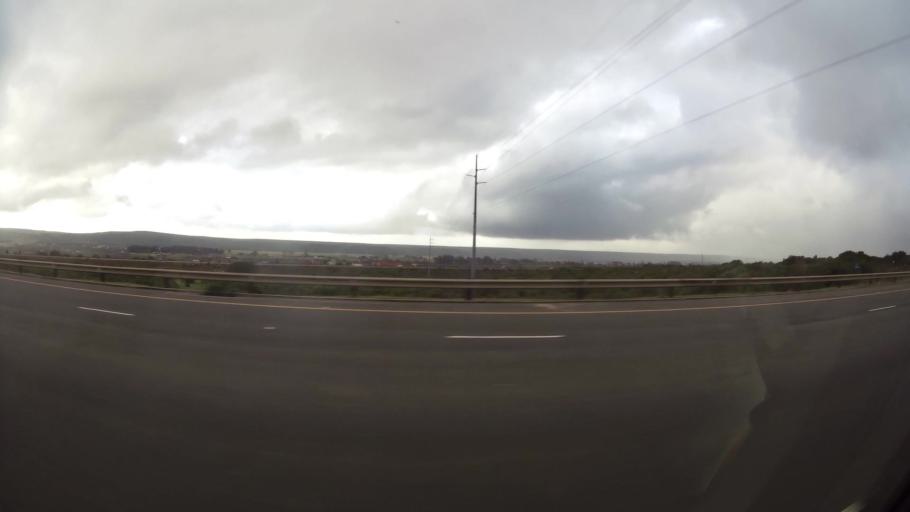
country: ZA
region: Eastern Cape
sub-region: Nelson Mandela Bay Metropolitan Municipality
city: Uitenhage
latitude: -33.8177
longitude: 25.5013
